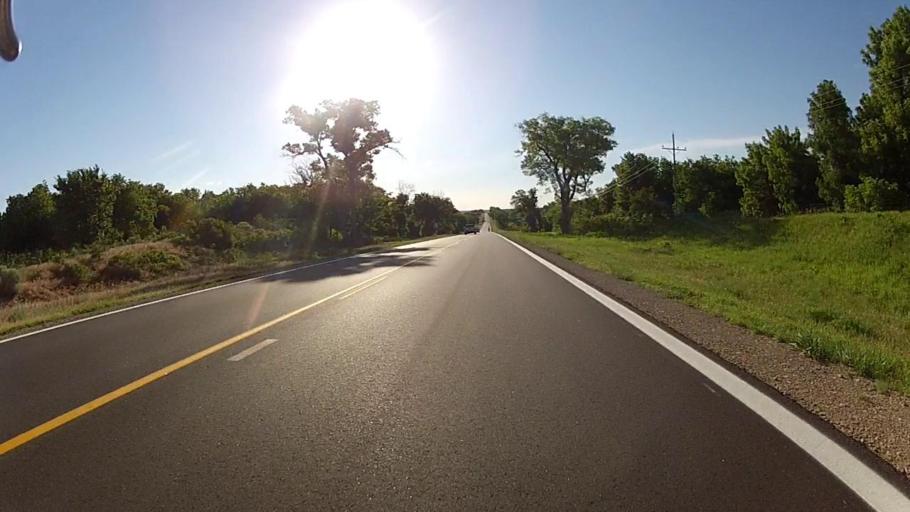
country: US
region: Kansas
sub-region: Comanche County
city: Coldwater
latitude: 37.2820
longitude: -99.0823
